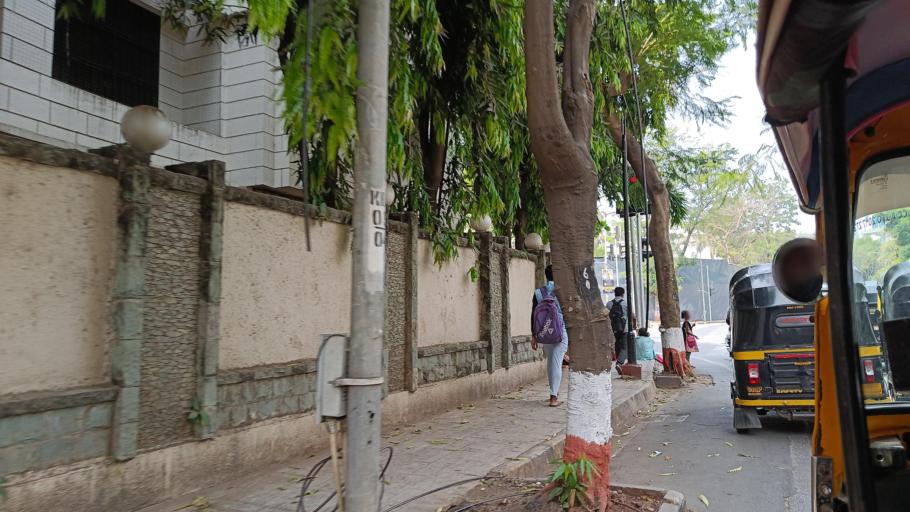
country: IN
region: Maharashtra
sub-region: Mumbai Suburban
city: Mumbai
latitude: 19.1071
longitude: 72.8303
